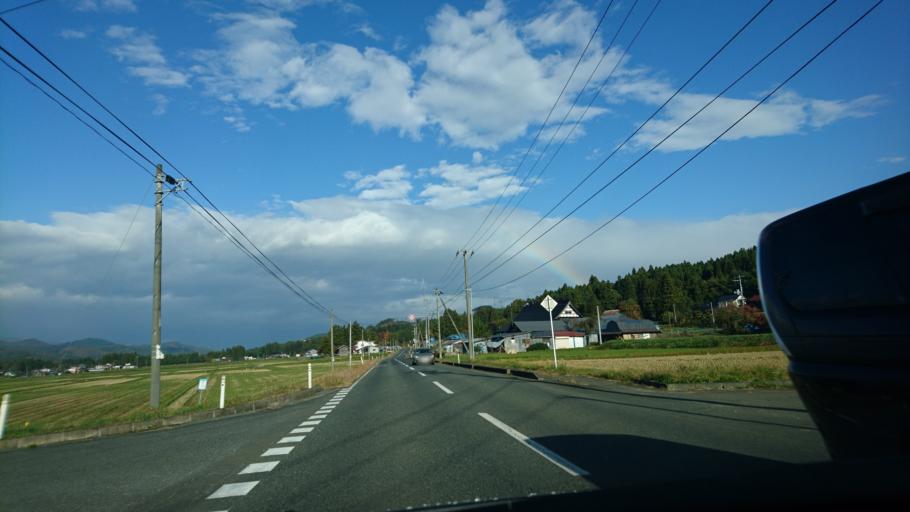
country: JP
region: Iwate
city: Mizusawa
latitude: 39.0286
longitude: 141.0820
